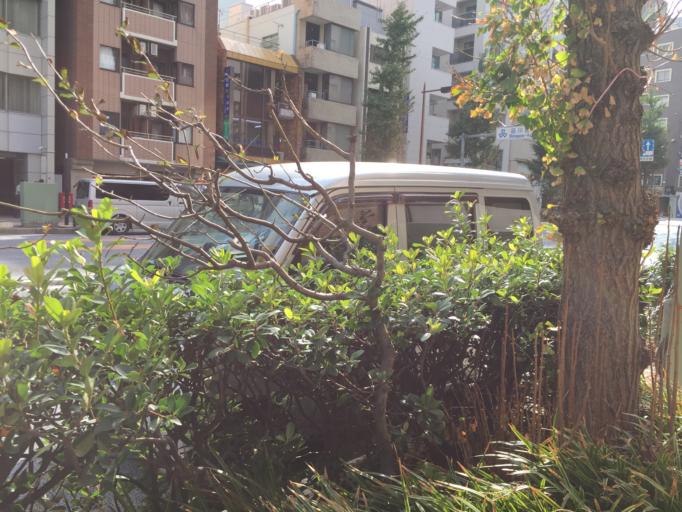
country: JP
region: Tokyo
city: Tokyo
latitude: 35.6347
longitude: 139.7192
